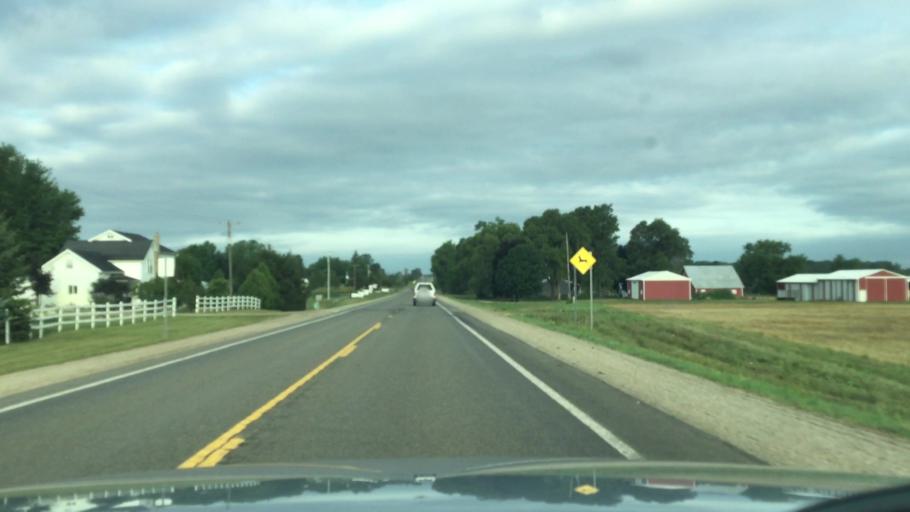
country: US
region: Michigan
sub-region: Montcalm County
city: Carson City
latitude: 43.1776
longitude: -84.9417
